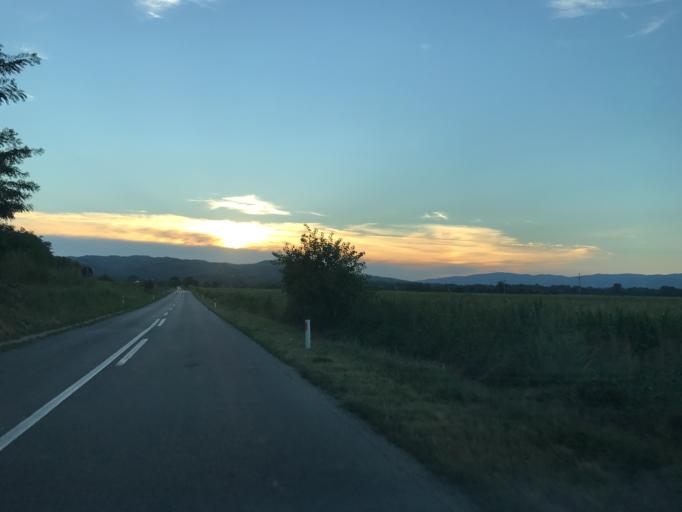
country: RS
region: Central Serbia
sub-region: Branicevski Okrug
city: Veliko Gradiste
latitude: 44.6956
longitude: 21.5531
